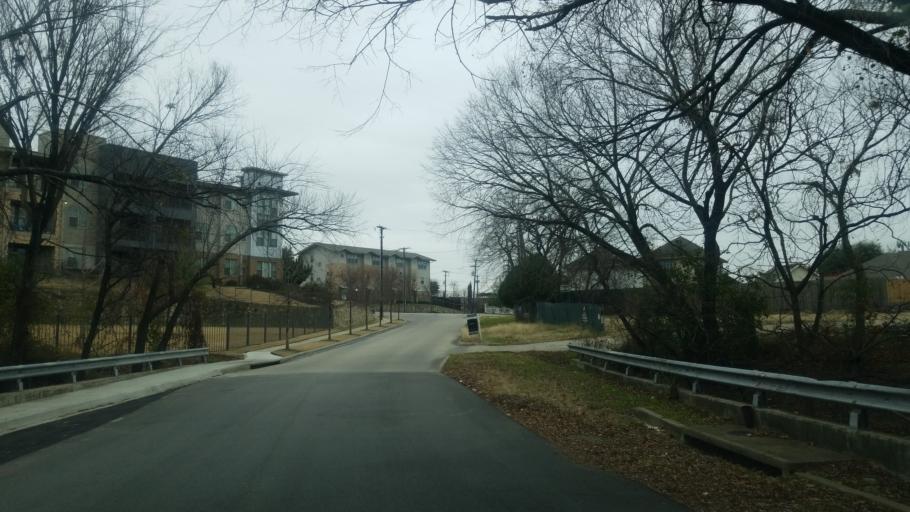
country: US
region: Texas
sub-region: Dallas County
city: Highland Park
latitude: 32.8166
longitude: -96.8261
